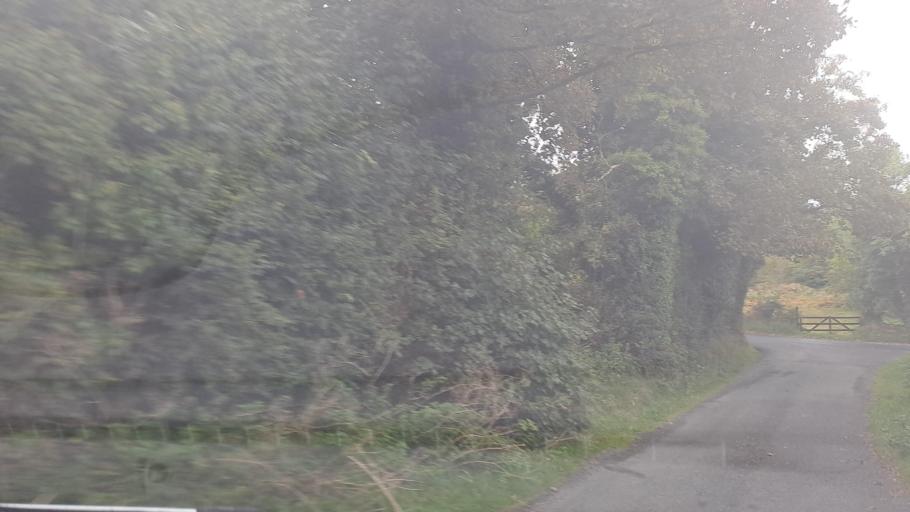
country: IE
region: Ulster
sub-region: County Monaghan
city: Carrickmacross
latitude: 53.9820
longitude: -6.7861
